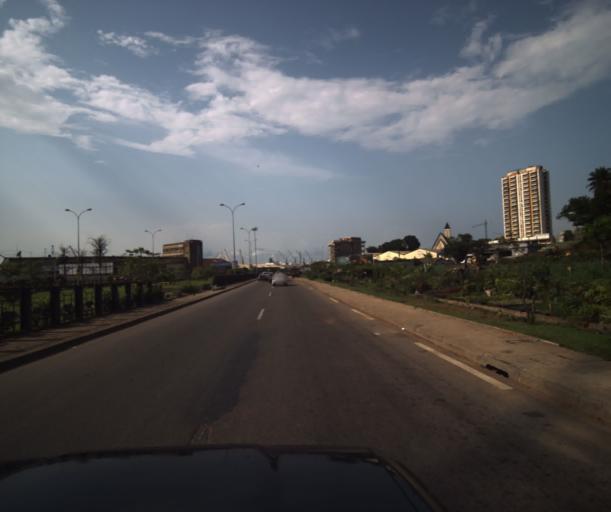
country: CM
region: Littoral
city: Douala
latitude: 4.0474
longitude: 9.6906
